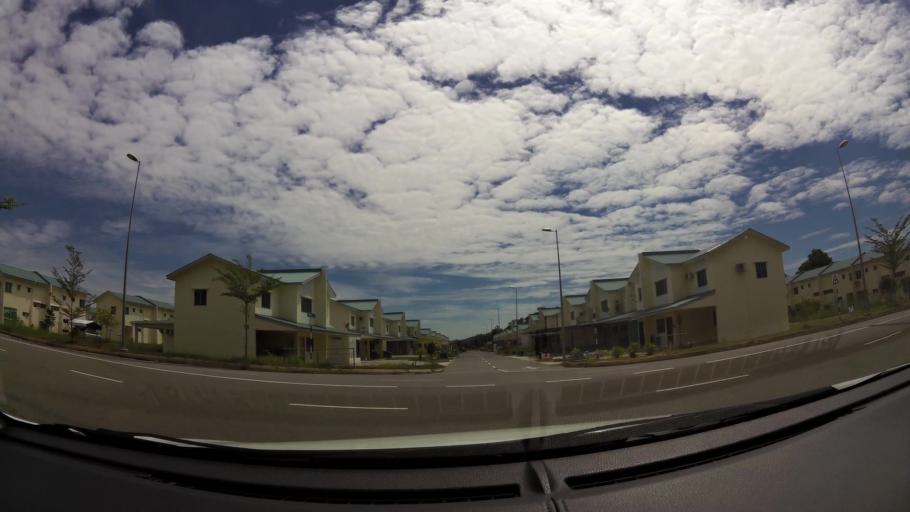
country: BN
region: Brunei and Muara
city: Bandar Seri Begawan
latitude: 4.9729
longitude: 115.0153
